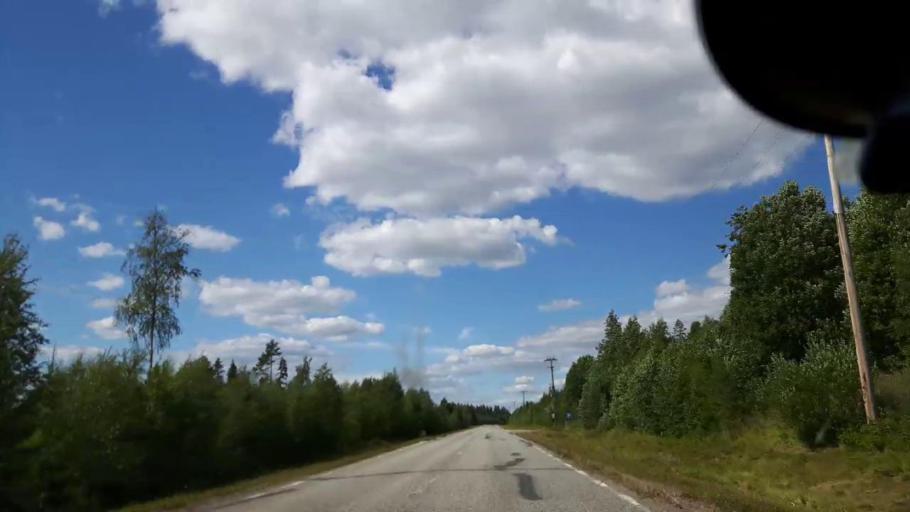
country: SE
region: Vaesternorrland
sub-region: Ange Kommun
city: Fransta
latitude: 62.7440
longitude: 16.3272
